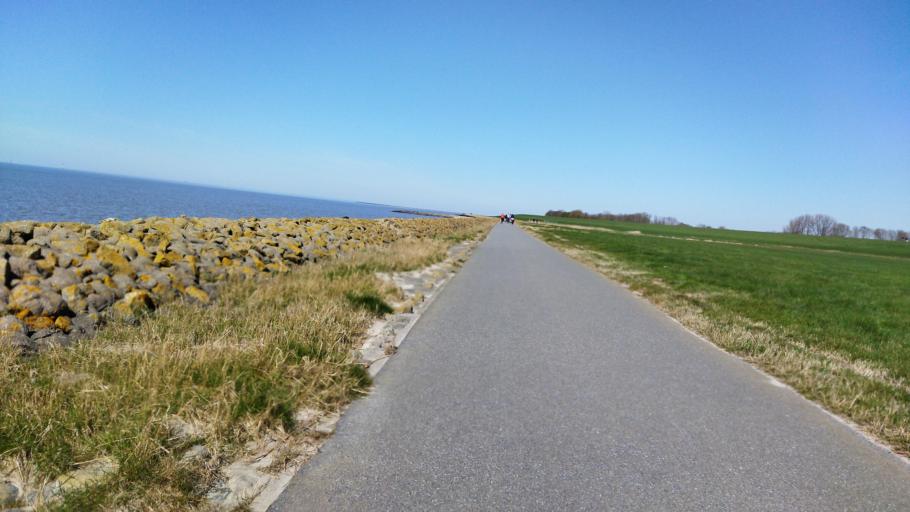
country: DE
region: Lower Saxony
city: Wremen
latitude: 53.6208
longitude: 8.5110
